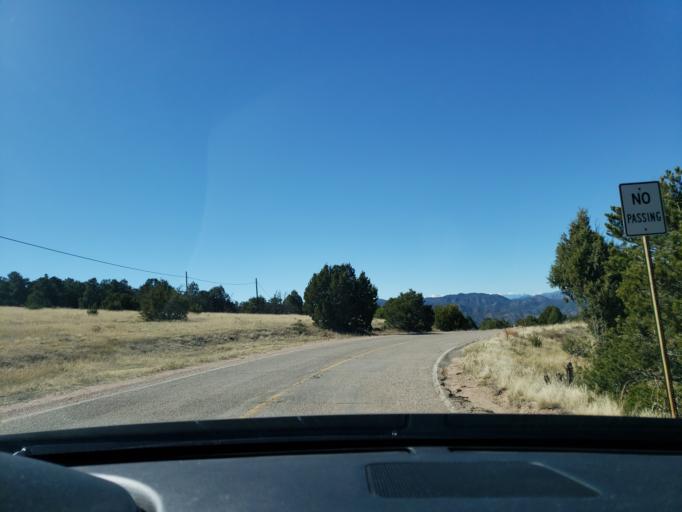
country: US
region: Colorado
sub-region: Fremont County
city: Canon City
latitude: 38.4648
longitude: -105.3096
